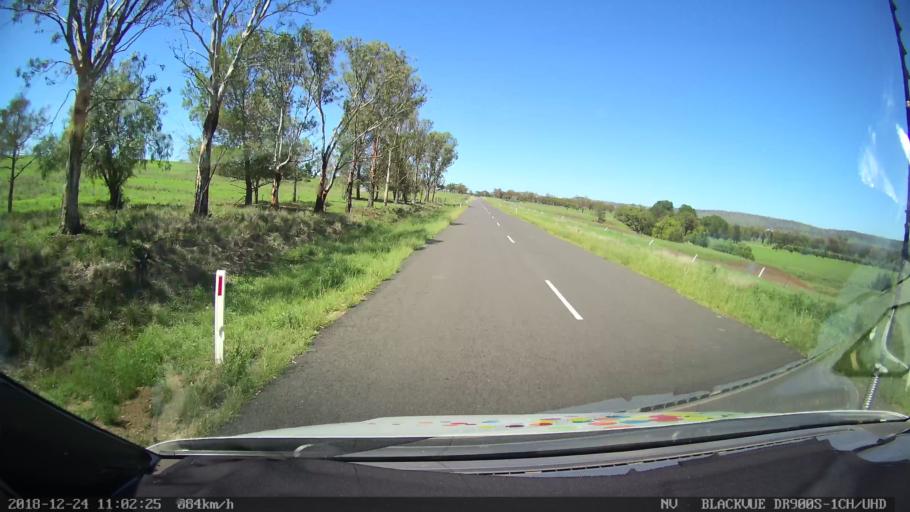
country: AU
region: New South Wales
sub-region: Upper Hunter Shire
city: Merriwa
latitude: -32.0848
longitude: 150.3753
